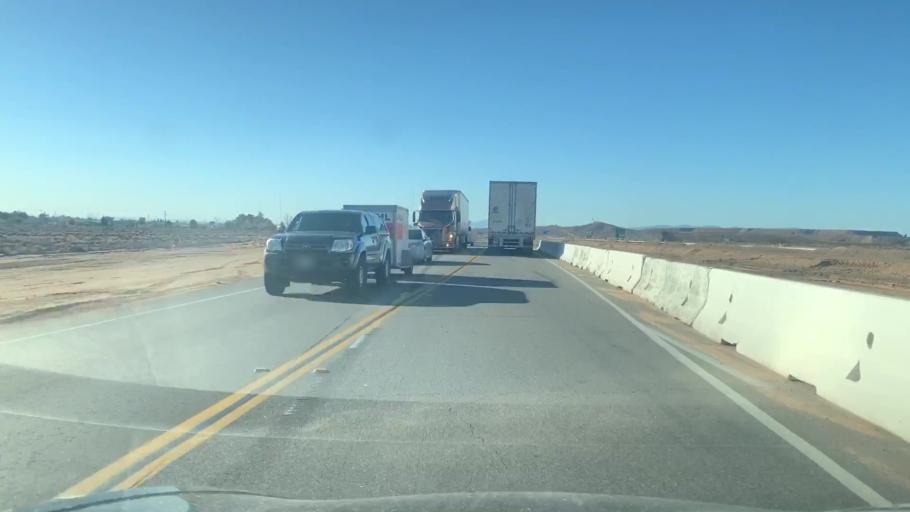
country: US
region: California
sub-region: Kern County
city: Boron
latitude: 35.0100
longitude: -117.6289
